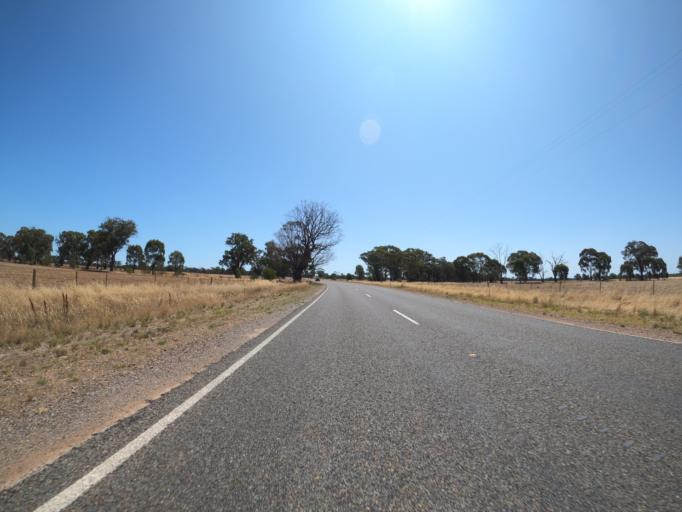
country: AU
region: New South Wales
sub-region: Corowa Shire
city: Corowa
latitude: -36.0655
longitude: 146.3768
